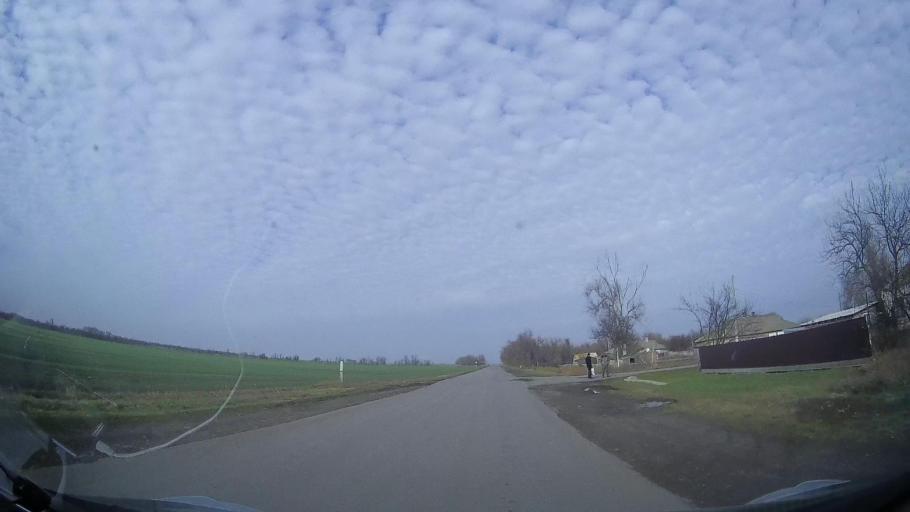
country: RU
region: Rostov
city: Gigant
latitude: 46.9242
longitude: 41.2473
